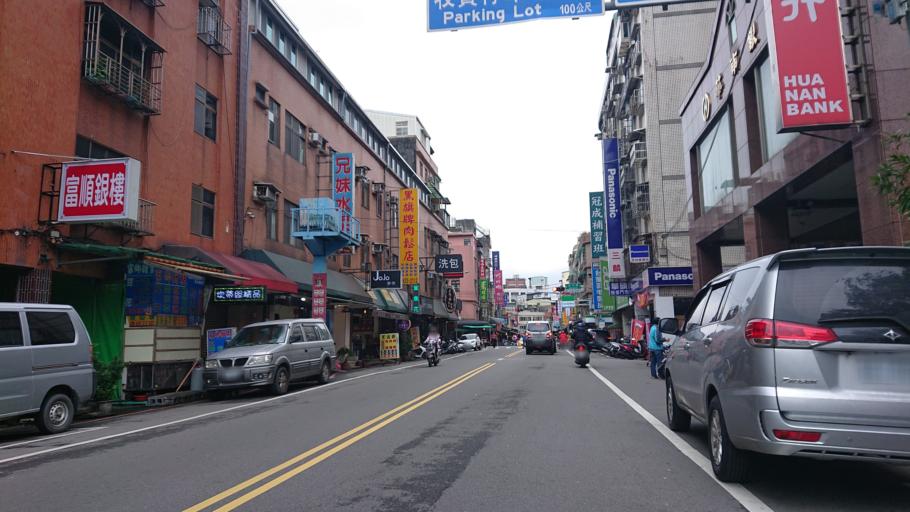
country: TW
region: Taiwan
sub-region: Taoyuan
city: Taoyuan
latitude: 24.9368
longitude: 121.3702
